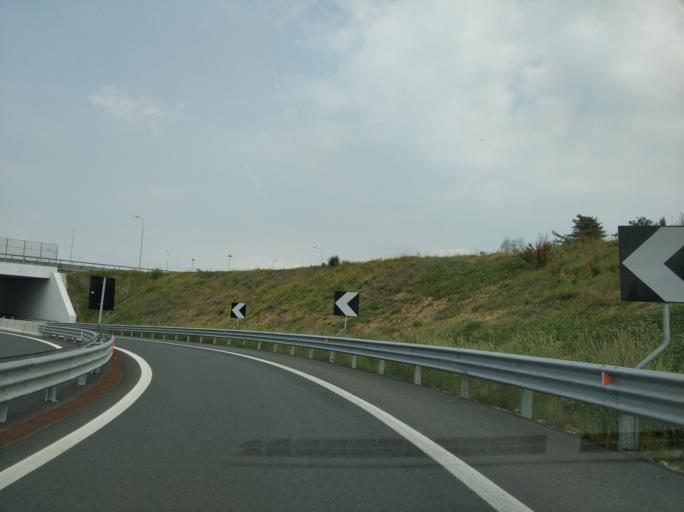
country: IT
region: Piedmont
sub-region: Provincia di Torino
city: San Giusto Canavese
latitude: 45.3160
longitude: 7.8218
